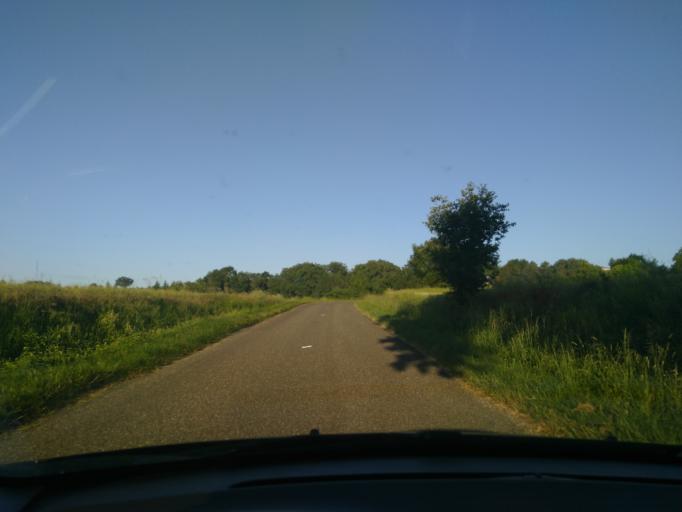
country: FR
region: Midi-Pyrenees
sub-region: Departement du Gers
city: Valence-sur-Baise
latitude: 43.8788
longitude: 0.4196
